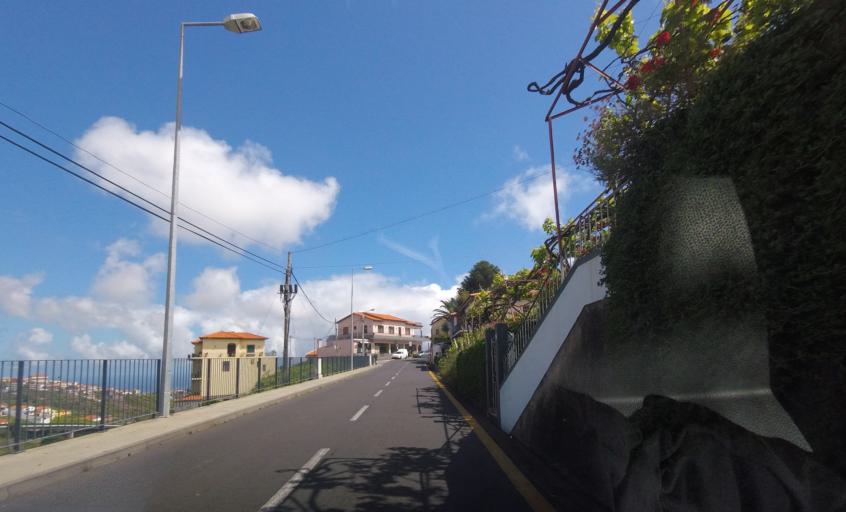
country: PT
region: Madeira
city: Camara de Lobos
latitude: 32.6735
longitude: -16.9782
